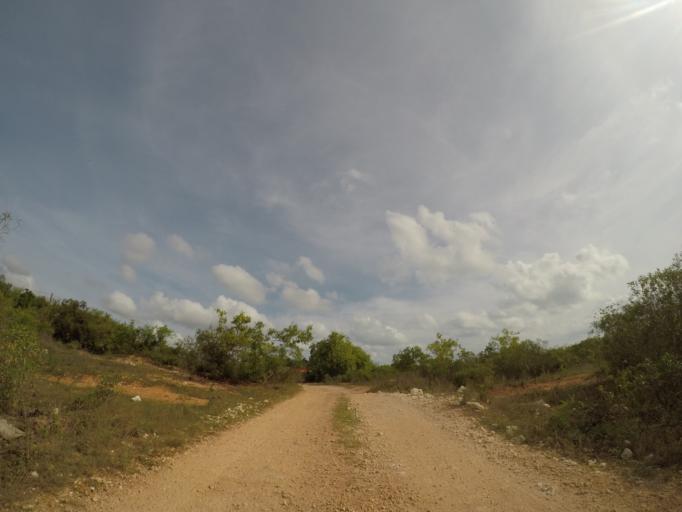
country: TZ
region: Zanzibar Central/South
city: Koani
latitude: -6.2312
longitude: 39.3208
